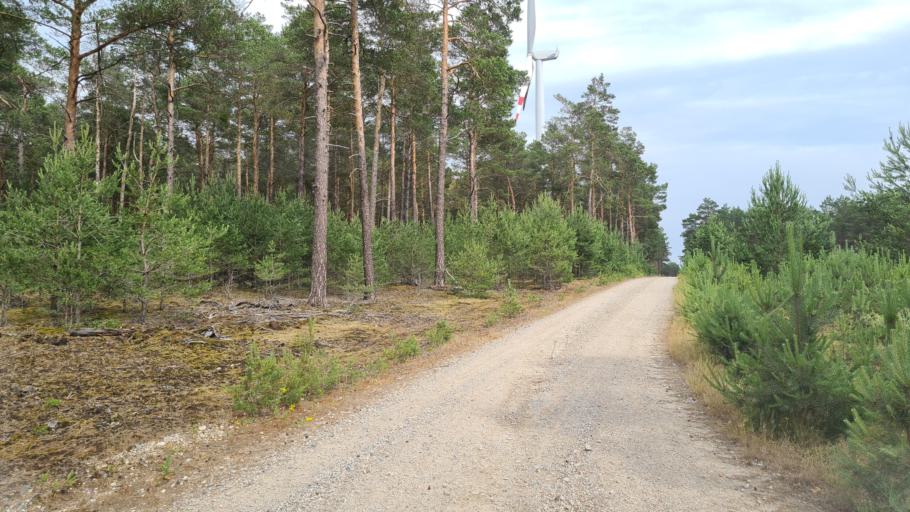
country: DE
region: Brandenburg
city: Schilda
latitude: 51.6573
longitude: 13.3415
